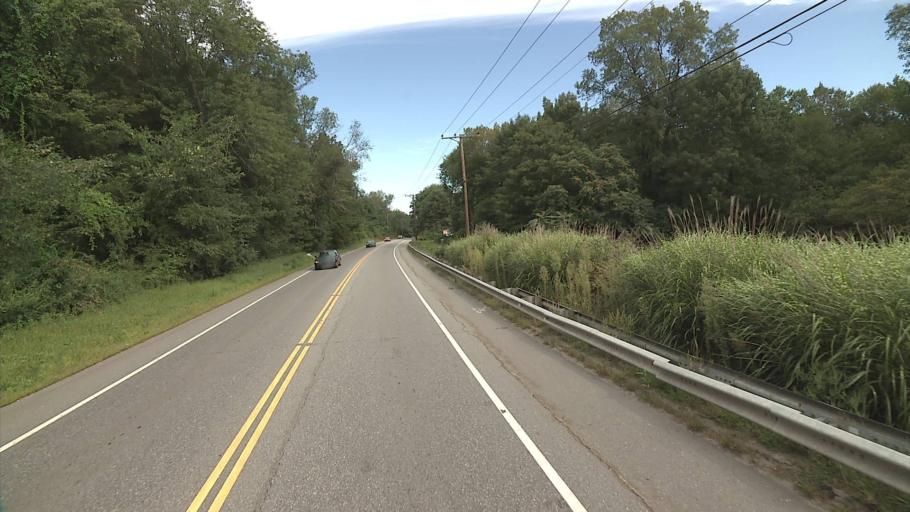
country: US
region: Connecticut
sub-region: Windham County
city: South Windham
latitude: 41.6611
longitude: -72.1598
